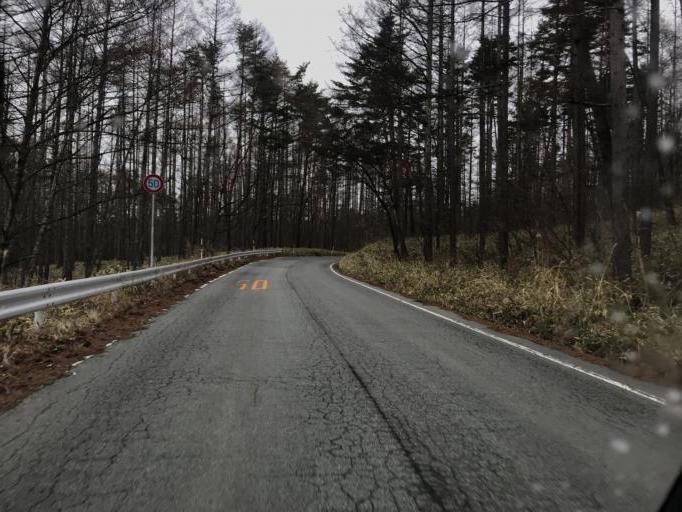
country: JP
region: Nagano
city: Chino
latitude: 35.8969
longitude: 138.3221
